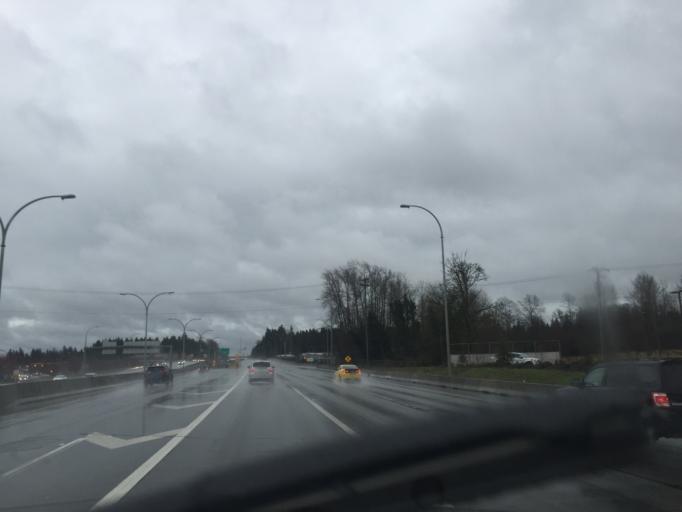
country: CA
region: British Columbia
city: Walnut Grove
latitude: 49.1632
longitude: -122.6655
